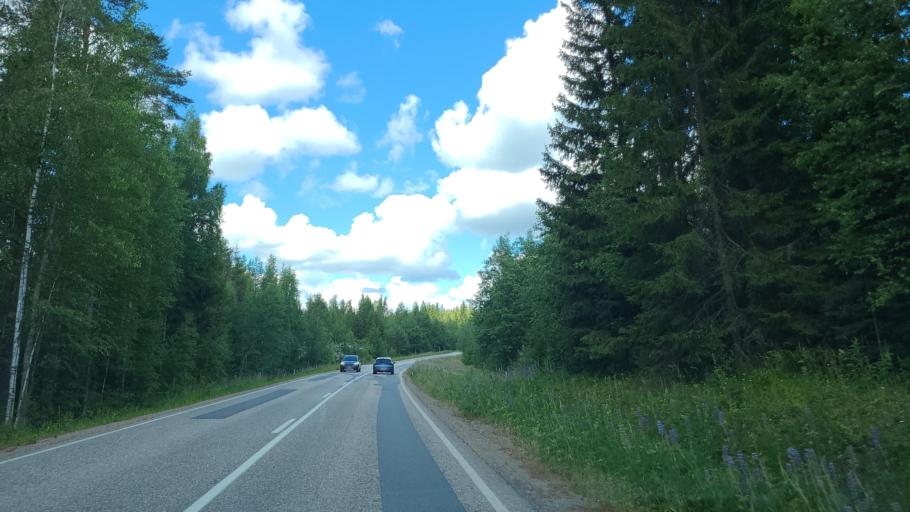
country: FI
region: Northern Savo
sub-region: Koillis-Savo
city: Kaavi
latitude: 62.9125
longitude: 28.7064
